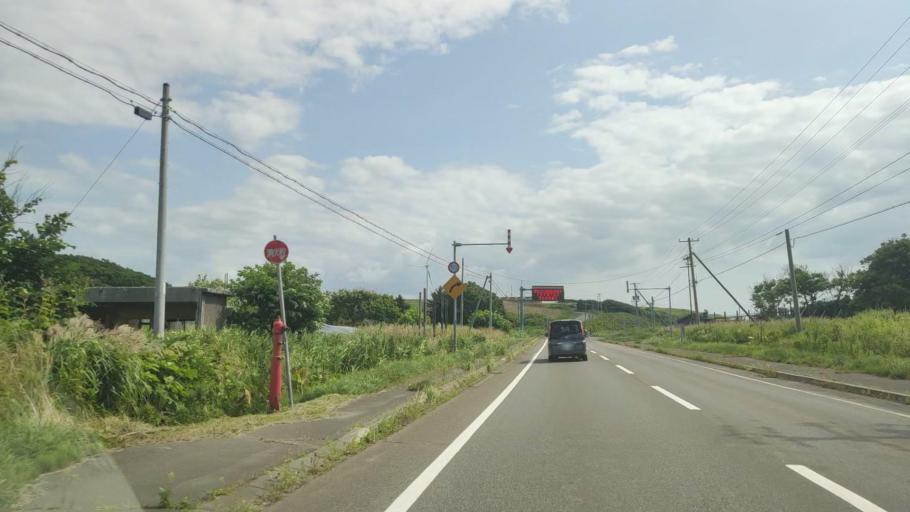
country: JP
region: Hokkaido
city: Rumoi
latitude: 44.2601
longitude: 141.6568
